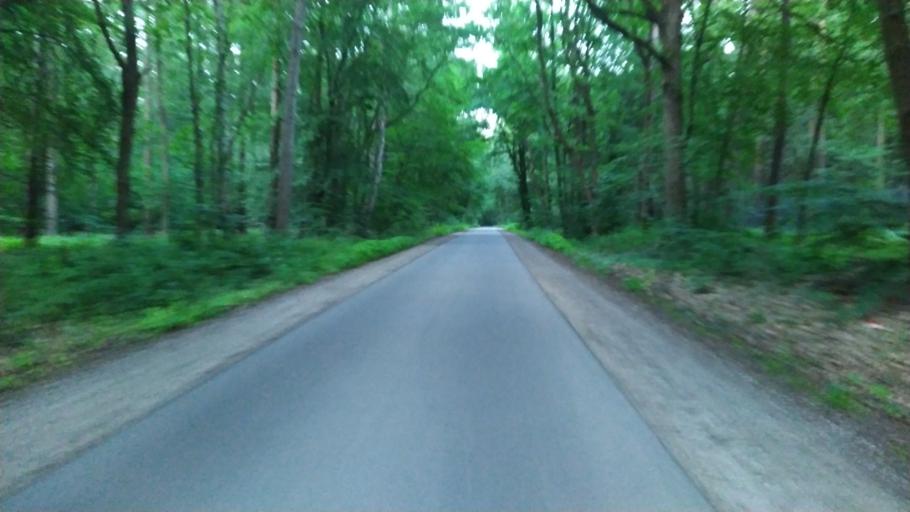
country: DE
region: Lower Saxony
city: Deinstedt
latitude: 53.4928
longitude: 9.2392
